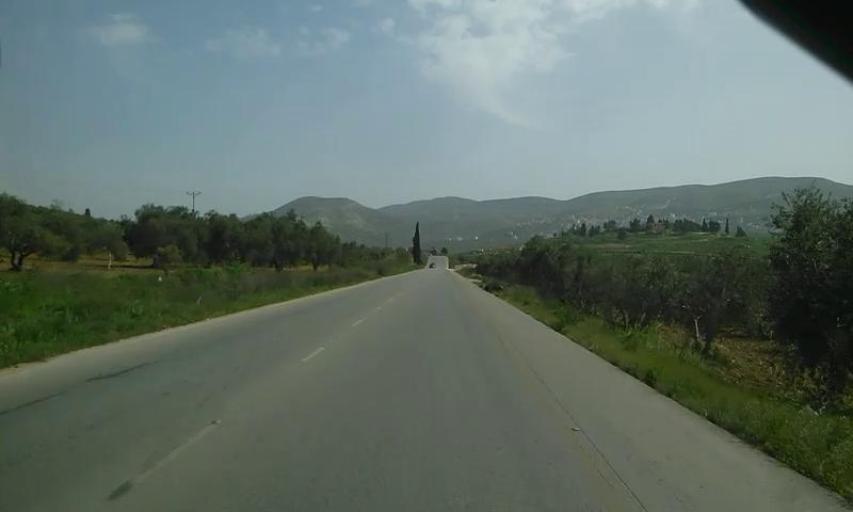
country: PS
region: West Bank
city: `Ajjah
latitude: 32.3434
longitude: 35.2018
